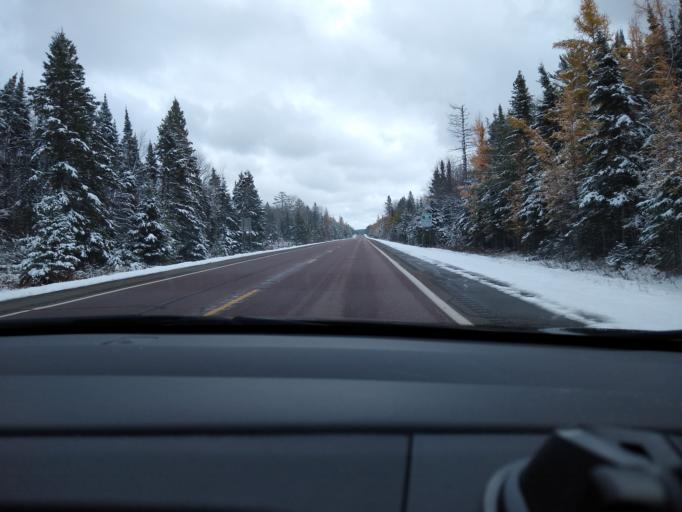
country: US
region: Michigan
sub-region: Iron County
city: Iron River
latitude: 46.1678
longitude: -88.9211
